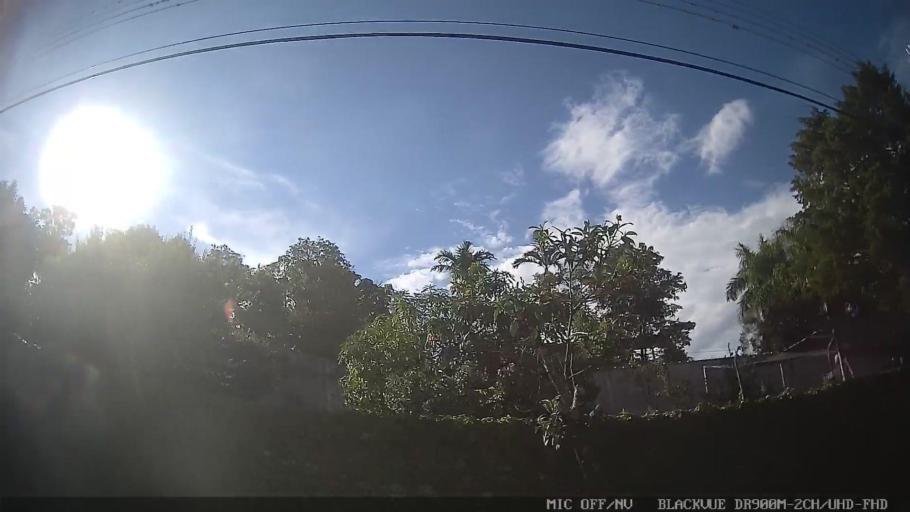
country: BR
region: Sao Paulo
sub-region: Serra Negra
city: Serra Negra
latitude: -22.6180
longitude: -46.7040
